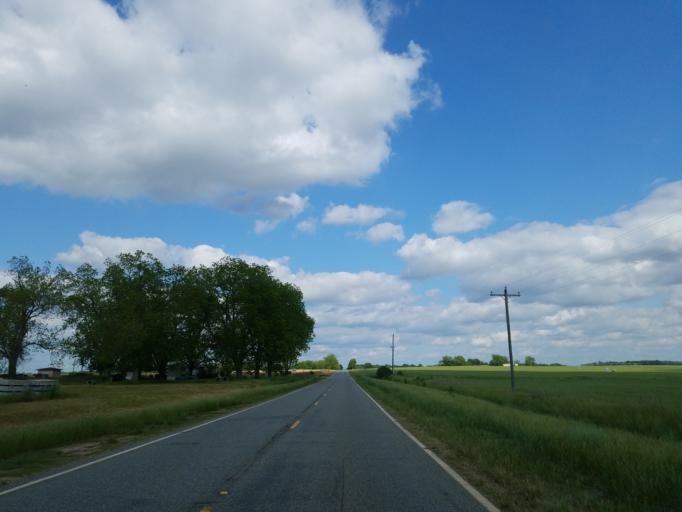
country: US
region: Georgia
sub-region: Dooly County
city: Unadilla
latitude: 32.2589
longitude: -83.7893
